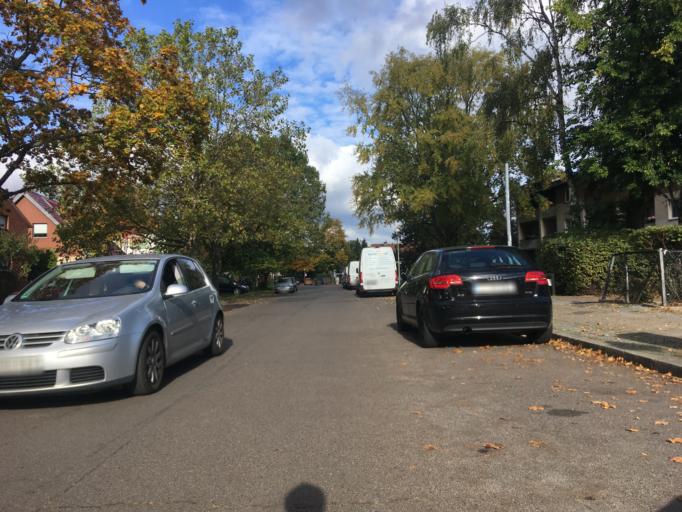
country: DE
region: Berlin
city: Rudow
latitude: 52.4239
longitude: 13.4953
